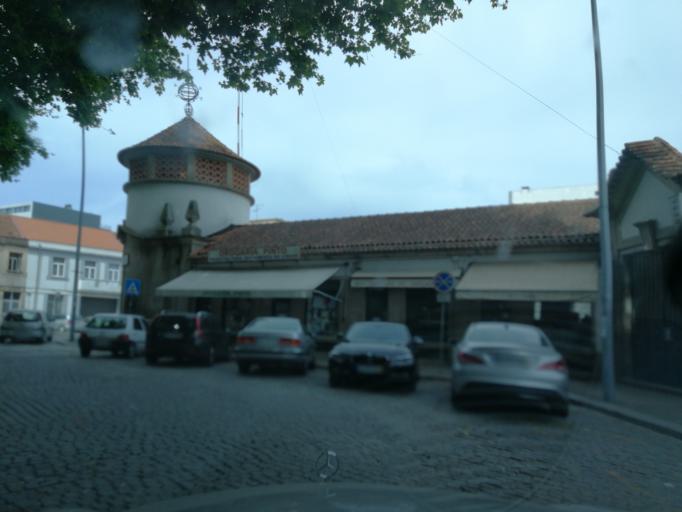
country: PT
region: Braga
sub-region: Vila Nova de Famalicao
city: Vila Nova de Famalicao
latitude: 41.4051
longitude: -8.5177
